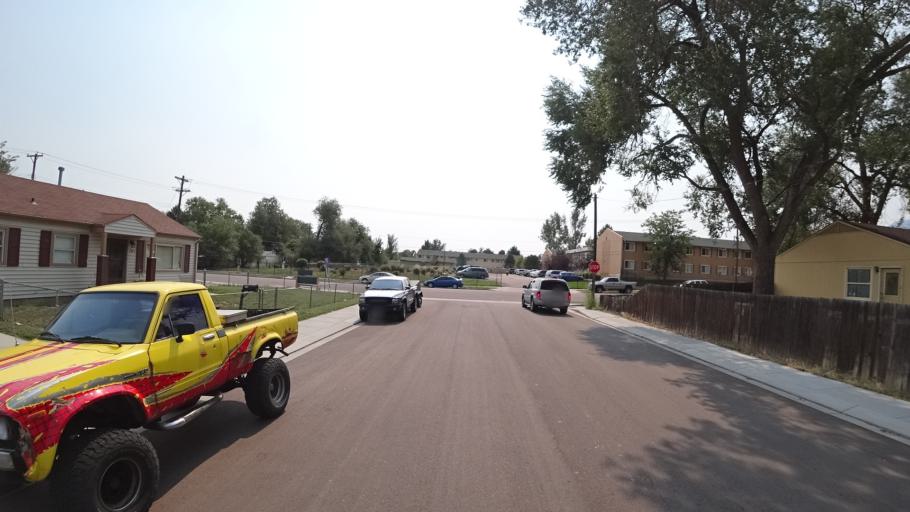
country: US
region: Colorado
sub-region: El Paso County
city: Colorado Springs
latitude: 38.8054
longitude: -104.8179
